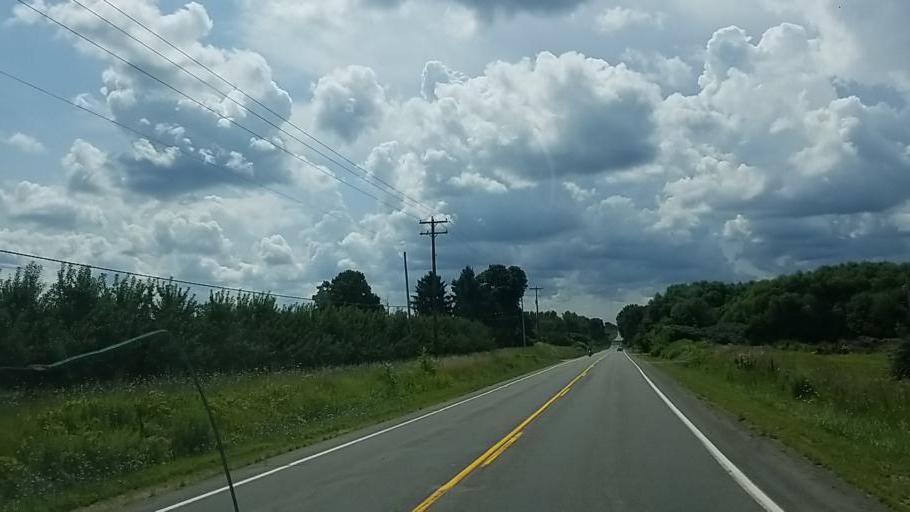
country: US
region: Michigan
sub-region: Kent County
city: Sparta
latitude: 43.1028
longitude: -85.7683
